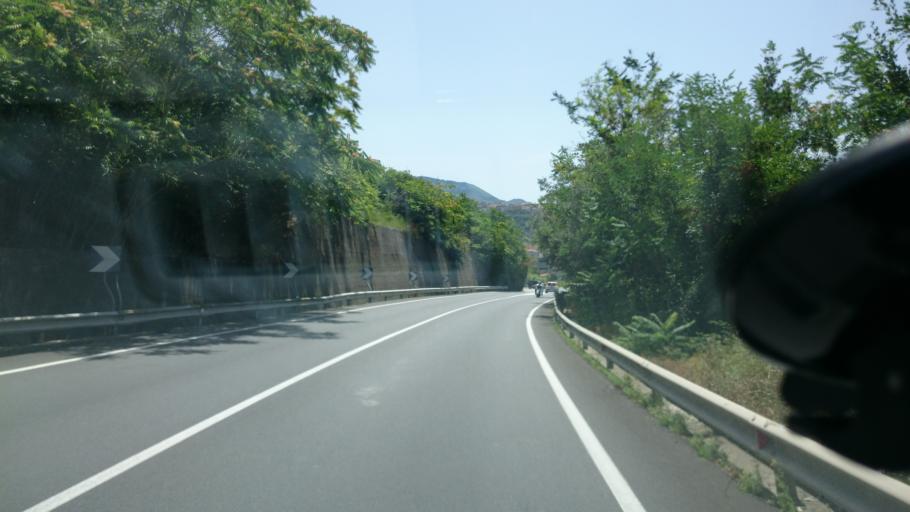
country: IT
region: Calabria
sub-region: Provincia di Cosenza
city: Cetraro Marina
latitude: 39.5294
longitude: 15.9249
